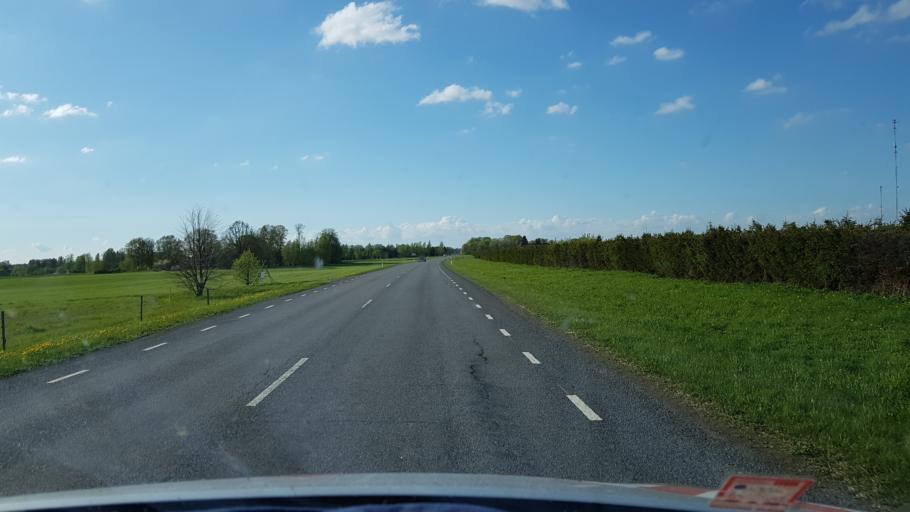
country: EE
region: Viljandimaa
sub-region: Suure-Jaani vald
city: Suure-Jaani
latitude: 58.4335
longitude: 25.4545
